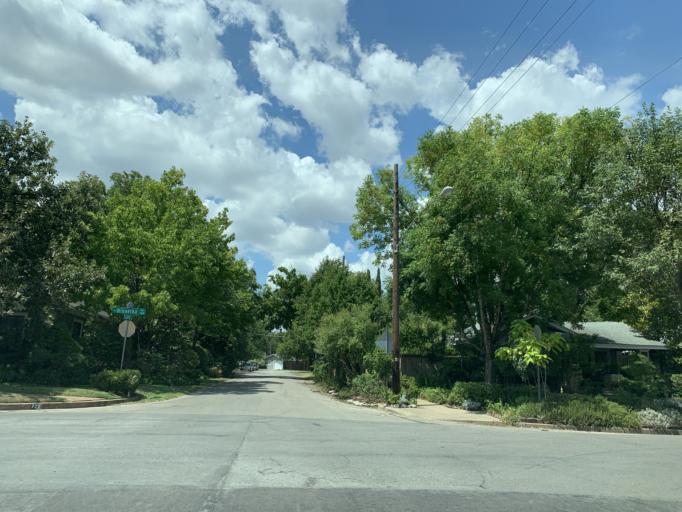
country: US
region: Texas
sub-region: Dallas County
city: Dallas
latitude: 32.7524
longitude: -96.8402
